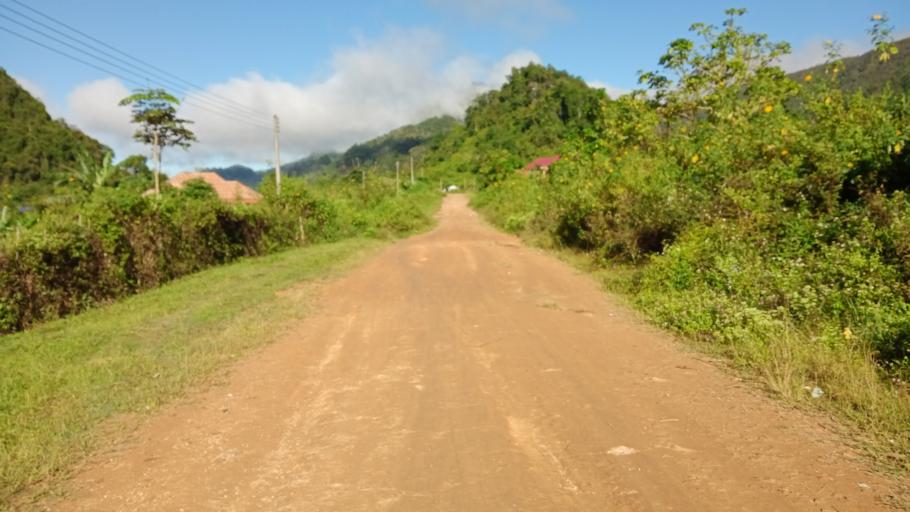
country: LA
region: Xiangkhoang
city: Phonsavan
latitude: 19.1152
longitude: 102.9118
